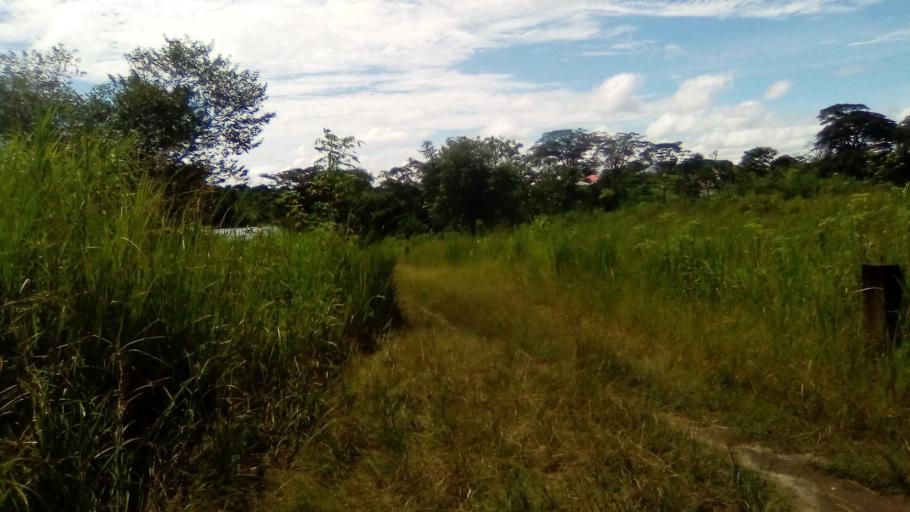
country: SL
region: Eastern Province
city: Simbakoro
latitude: 8.6356
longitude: -11.0004
